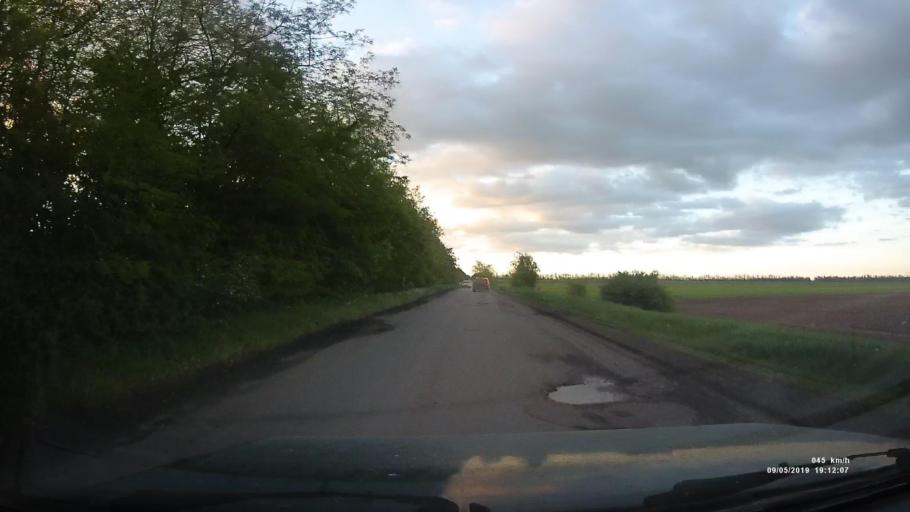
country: RU
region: Krasnodarskiy
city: Kanelovskaya
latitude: 46.7396
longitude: 39.2136
